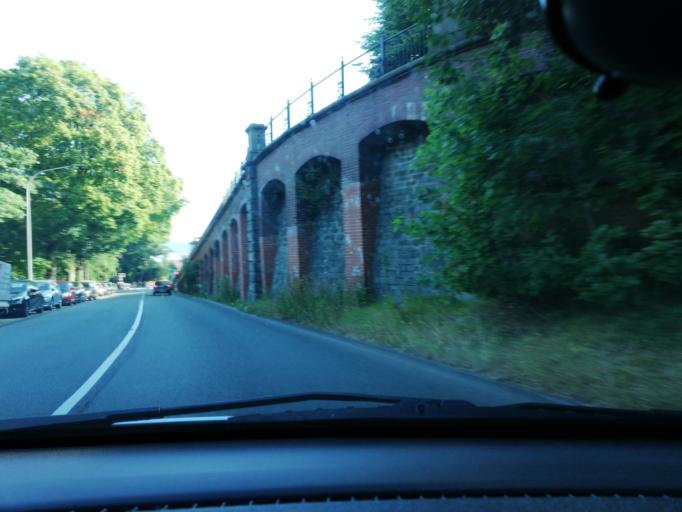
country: DE
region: North Rhine-Westphalia
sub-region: Regierungsbezirk Dusseldorf
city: Wuppertal
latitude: 51.2658
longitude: 7.2066
